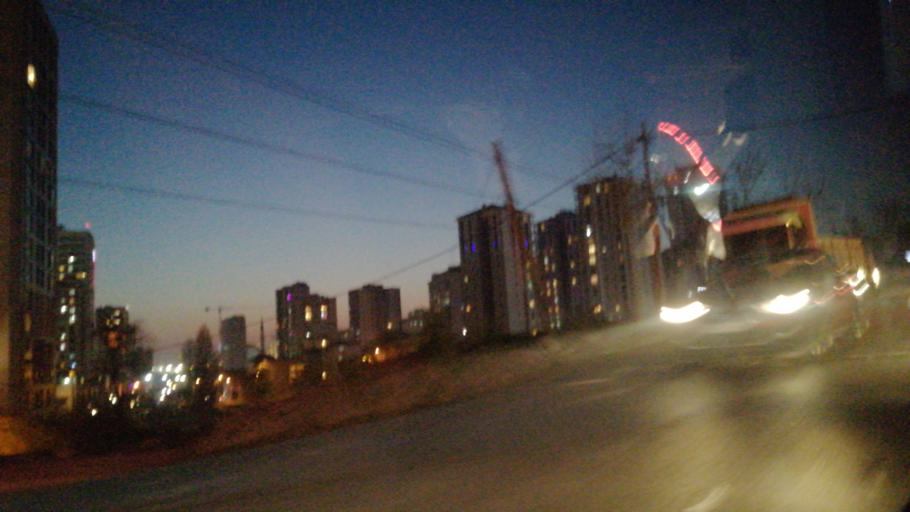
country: TR
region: Istanbul
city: Umraniye
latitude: 41.0019
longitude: 29.1384
